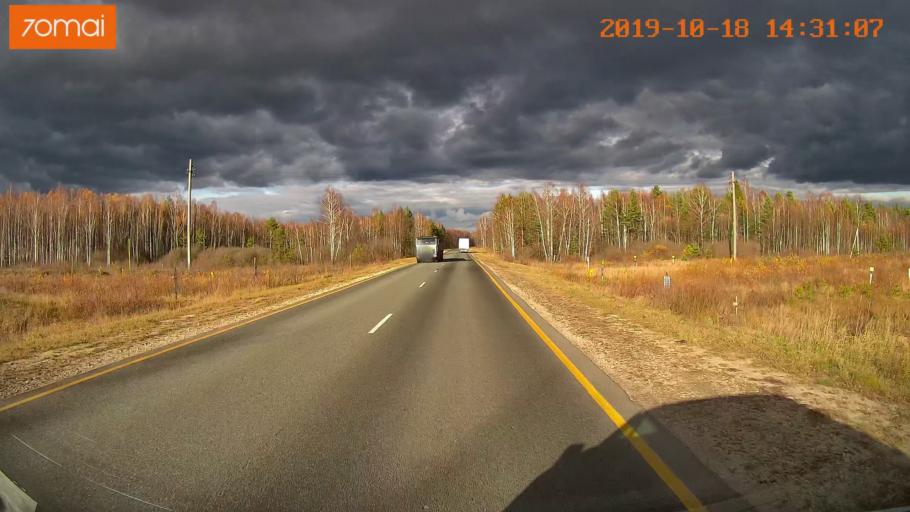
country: RU
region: Rjazan
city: Tuma
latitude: 55.1784
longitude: 40.5684
